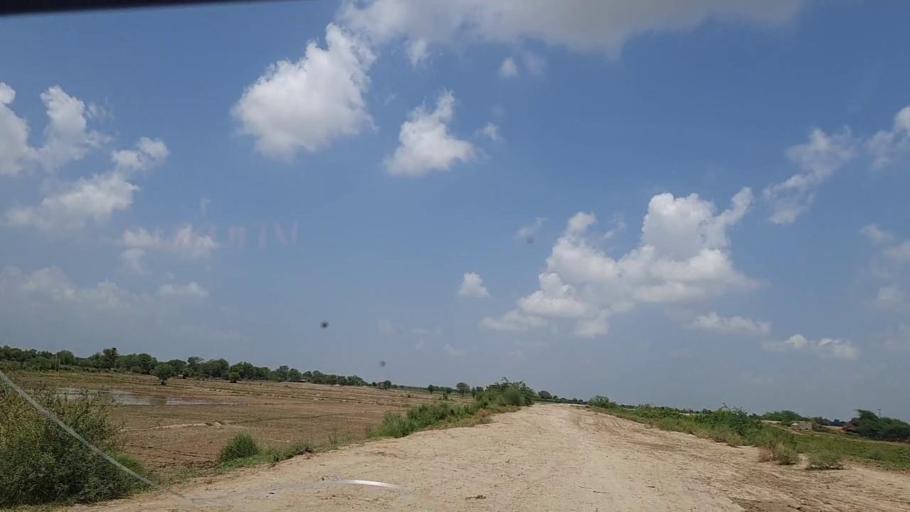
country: PK
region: Sindh
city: Tharu Shah
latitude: 26.9451
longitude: 68.0141
